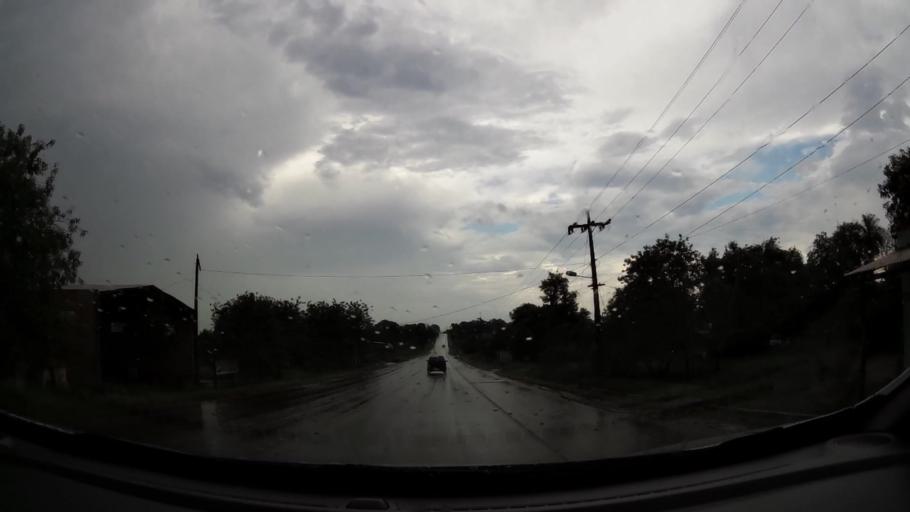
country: PY
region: Alto Parana
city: Presidente Franco
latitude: -25.5626
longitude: -54.6650
